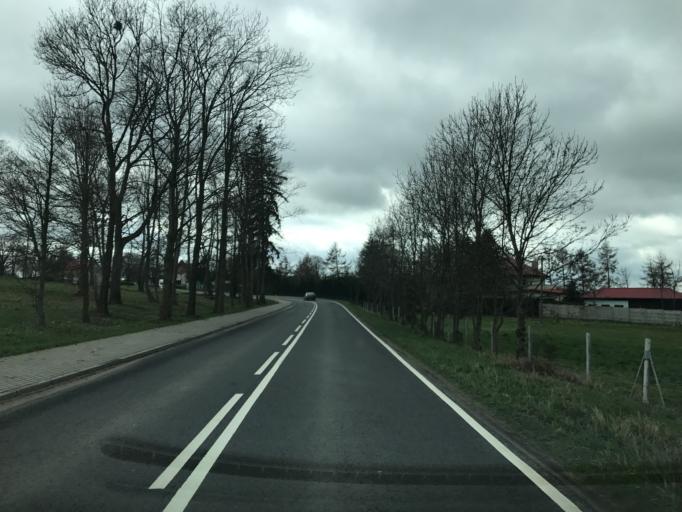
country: PL
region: Warmian-Masurian Voivodeship
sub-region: Powiat ostrodzki
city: Gierzwald
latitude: 53.4970
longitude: 20.1388
